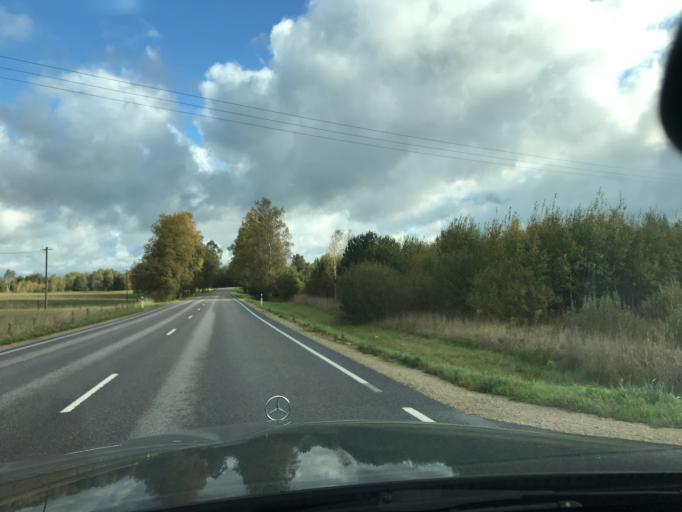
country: EE
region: Valgamaa
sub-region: Torva linn
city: Torva
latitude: 58.0277
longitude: 25.8315
